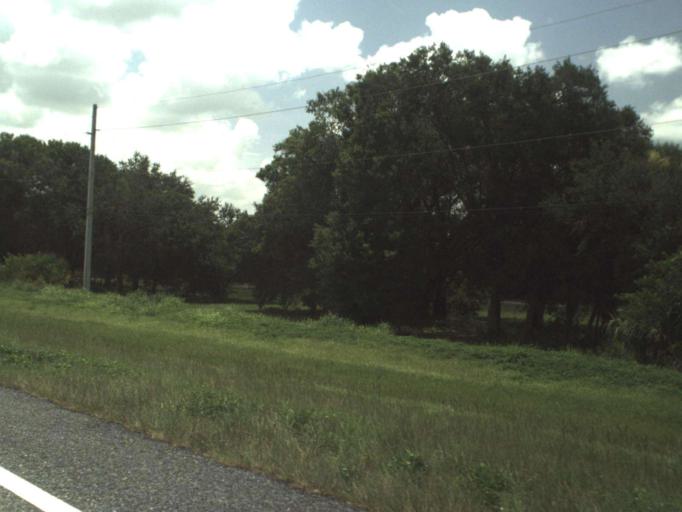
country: US
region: Florida
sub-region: Saint Lucie County
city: Fort Pierce South
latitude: 27.3686
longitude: -80.5554
